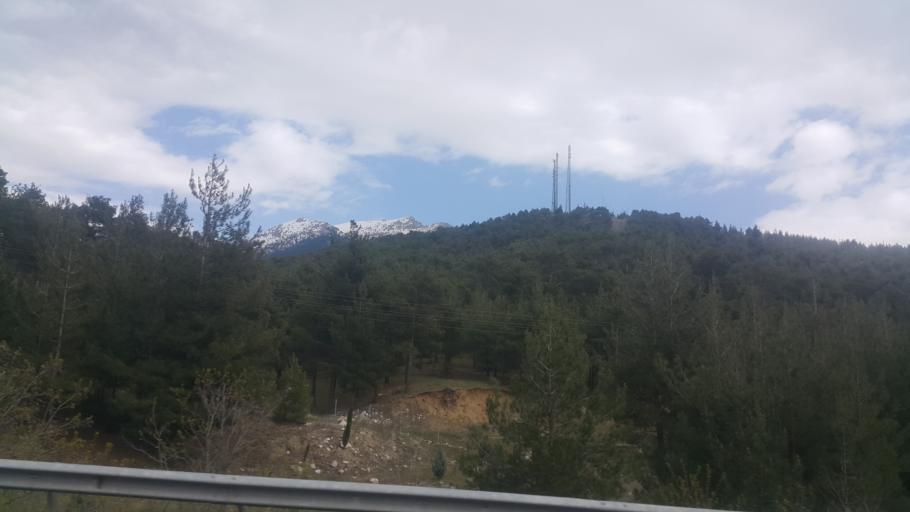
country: TR
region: Adana
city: Pozanti
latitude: 37.4261
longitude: 34.8778
